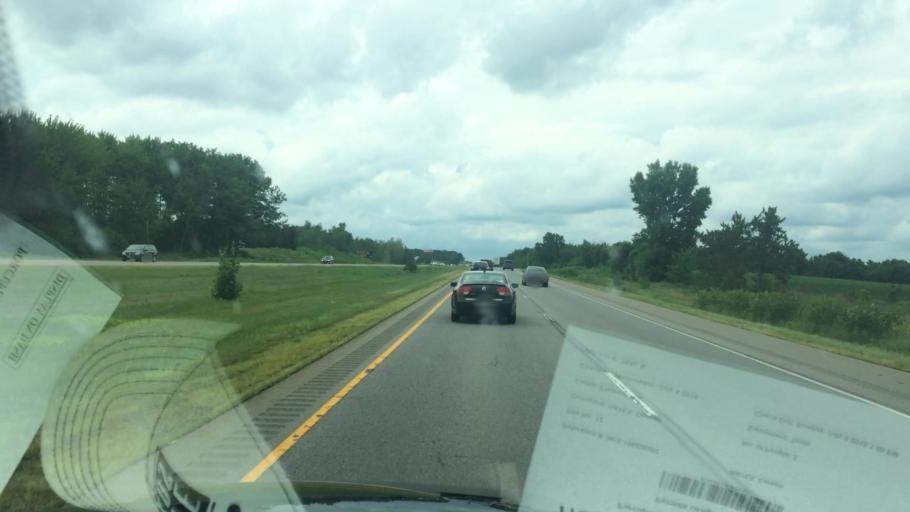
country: US
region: Wisconsin
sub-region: Marathon County
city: Mosinee
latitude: 44.7492
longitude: -89.6797
